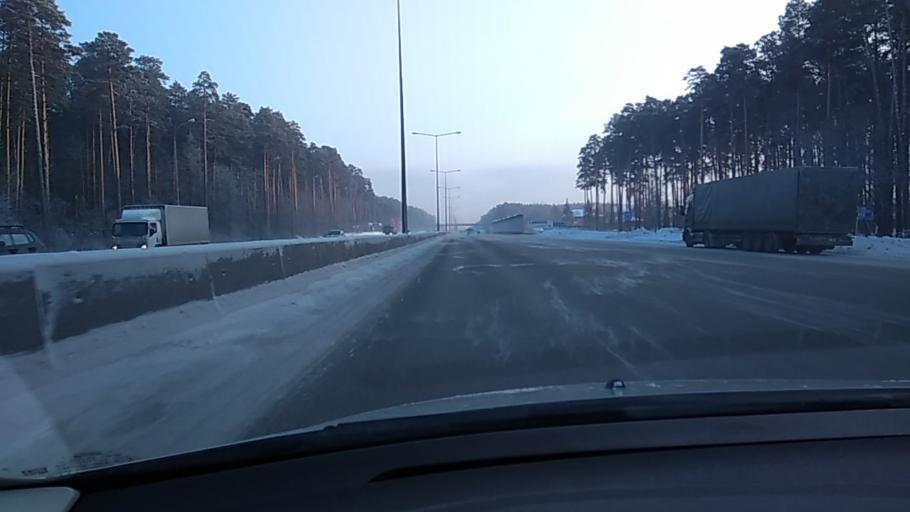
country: RU
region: Sverdlovsk
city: Yekaterinburg
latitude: 56.7902
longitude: 60.6707
